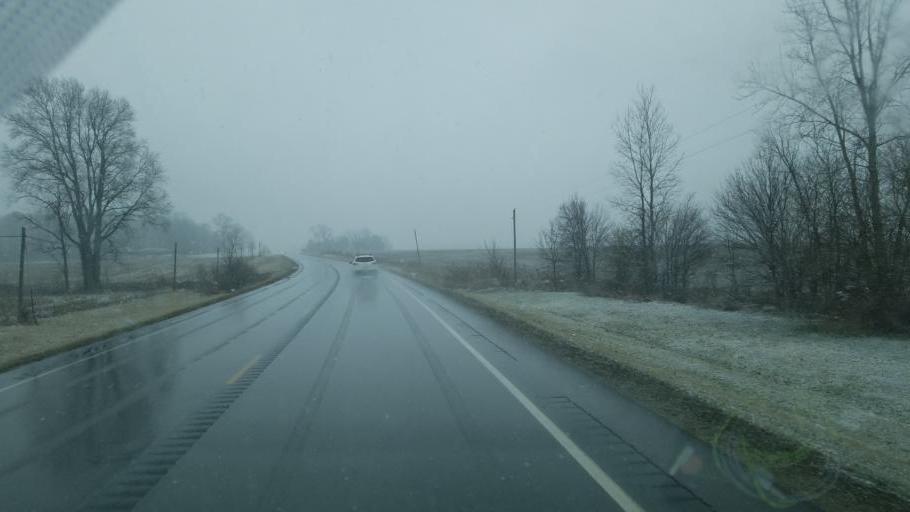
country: US
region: Indiana
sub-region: Grant County
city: Sweetser
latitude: 40.6381
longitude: -85.7091
